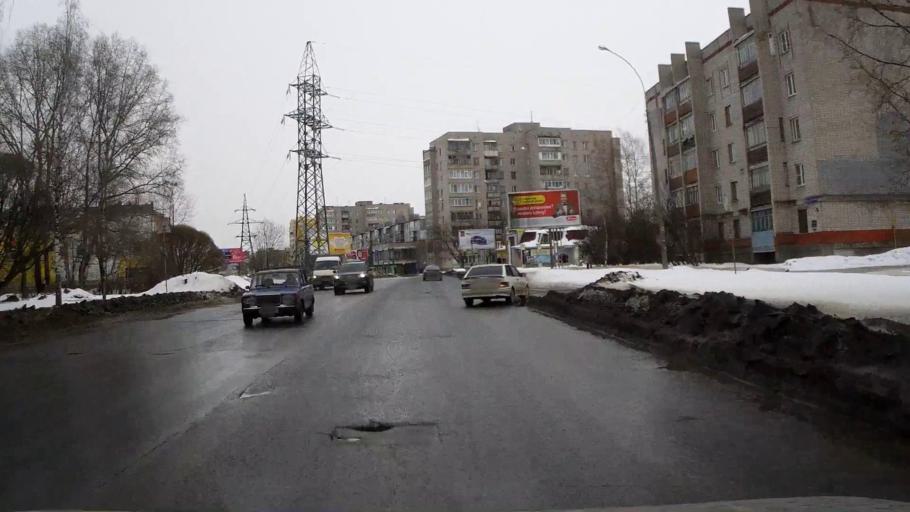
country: RU
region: Vologda
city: Vologda
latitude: 59.2164
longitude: 39.9197
